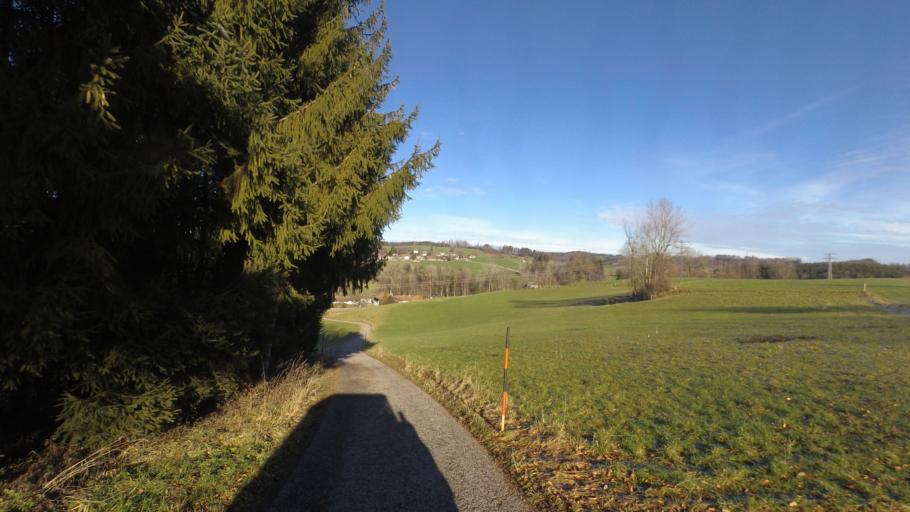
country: DE
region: Bavaria
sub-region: Upper Bavaria
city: Bergen
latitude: 47.8427
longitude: 12.5792
